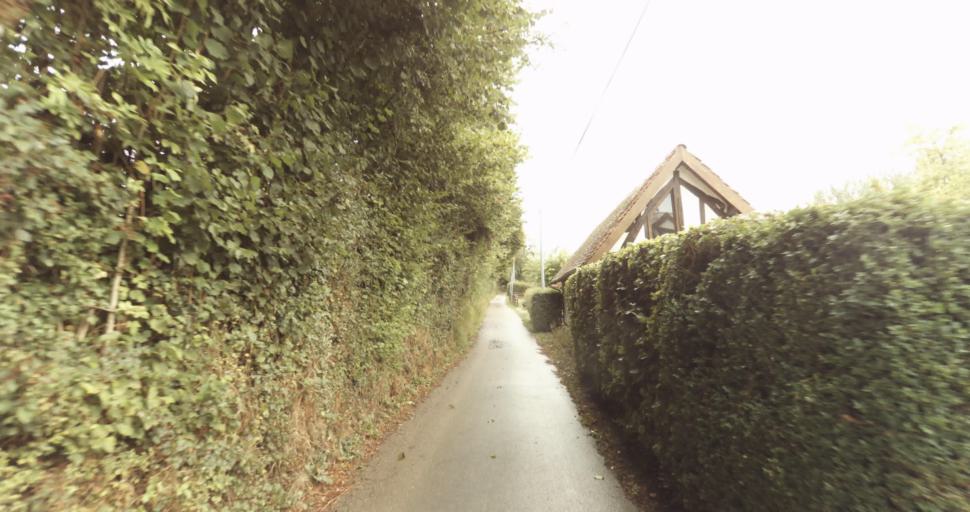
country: FR
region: Lower Normandy
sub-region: Departement de l'Orne
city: Vimoutiers
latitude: 48.8514
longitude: 0.2268
